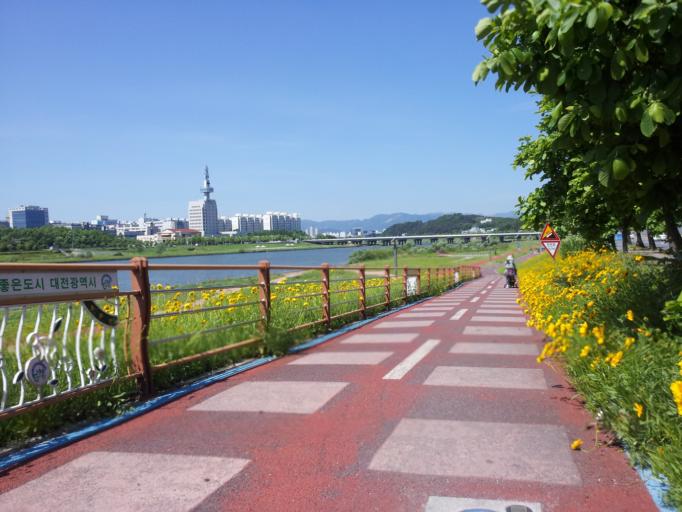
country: KR
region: Daejeon
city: Songgang-dong
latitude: 36.3741
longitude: 127.3876
